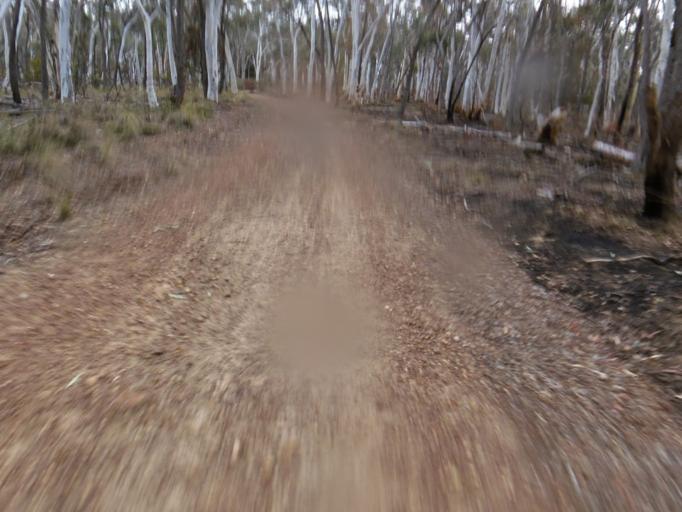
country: AU
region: Australian Capital Territory
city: Acton
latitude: -35.2638
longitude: 149.0986
